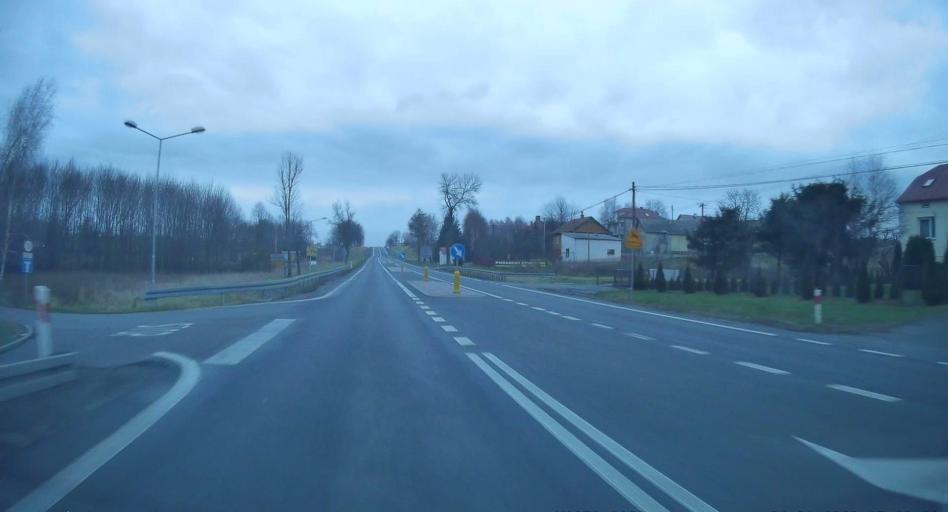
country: PL
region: Subcarpathian Voivodeship
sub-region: Powiat ropczycko-sedziszowski
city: Ropczyce
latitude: 50.0612
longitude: 21.6404
